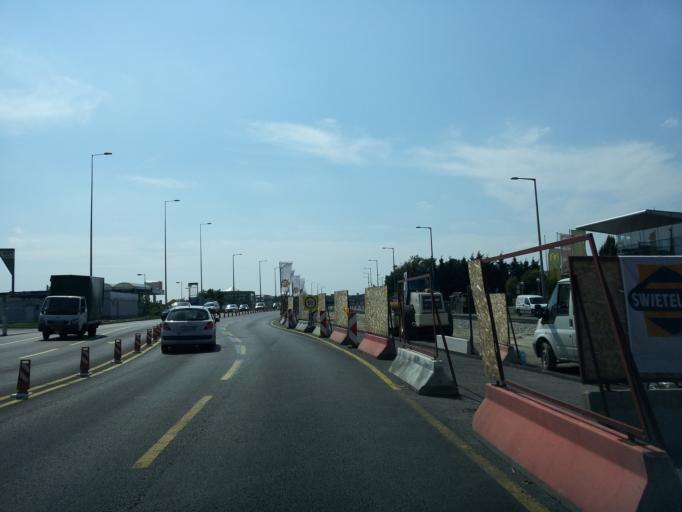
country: HU
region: Budapest
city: Budapest XI. keruelet
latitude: 47.4650
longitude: 19.0142
